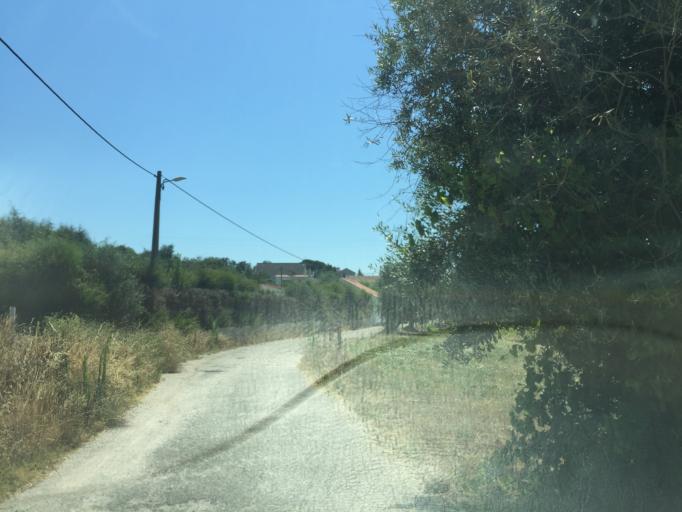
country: PT
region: Santarem
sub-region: Ferreira do Zezere
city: Ferreira do Zezere
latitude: 39.6203
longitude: -8.3130
